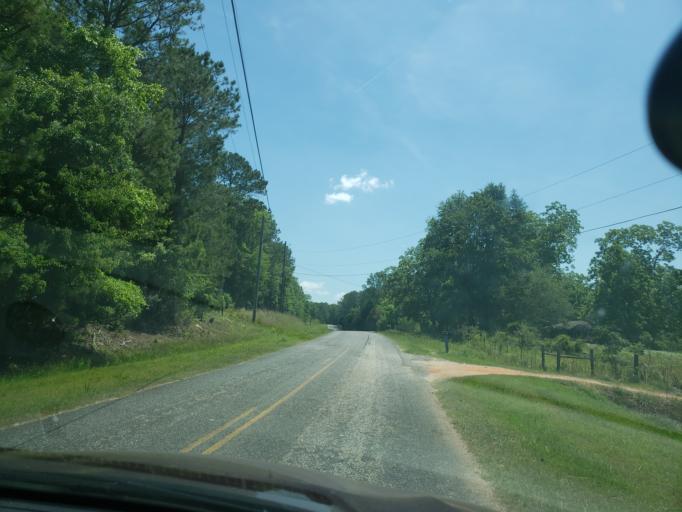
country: US
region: Alabama
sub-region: Elmore County
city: Tallassee
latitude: 32.5889
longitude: -85.8657
